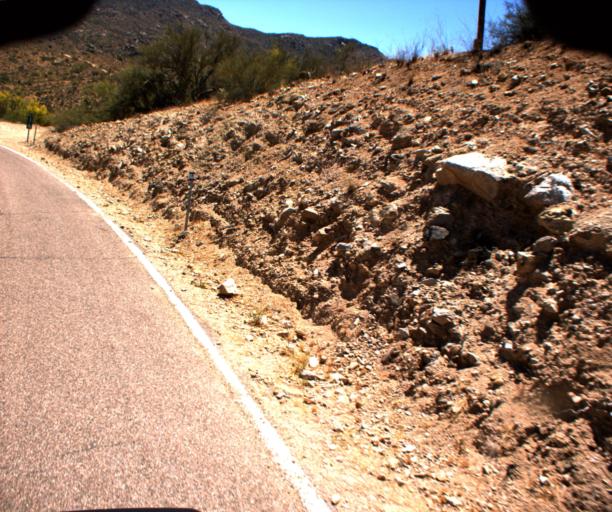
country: US
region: Arizona
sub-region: Yavapai County
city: Bagdad
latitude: 34.4575
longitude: -112.9988
